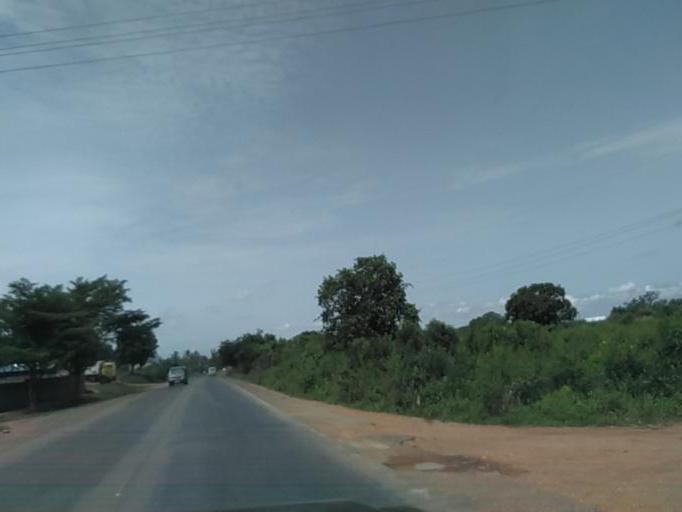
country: GH
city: Akropong
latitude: 6.1785
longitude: 0.0716
